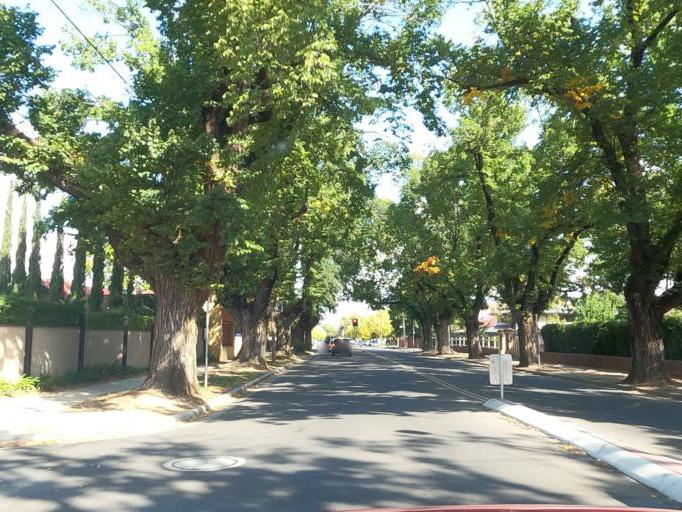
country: AU
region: New South Wales
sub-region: Albury Municipality
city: Albury
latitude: -36.0733
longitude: 146.9170
